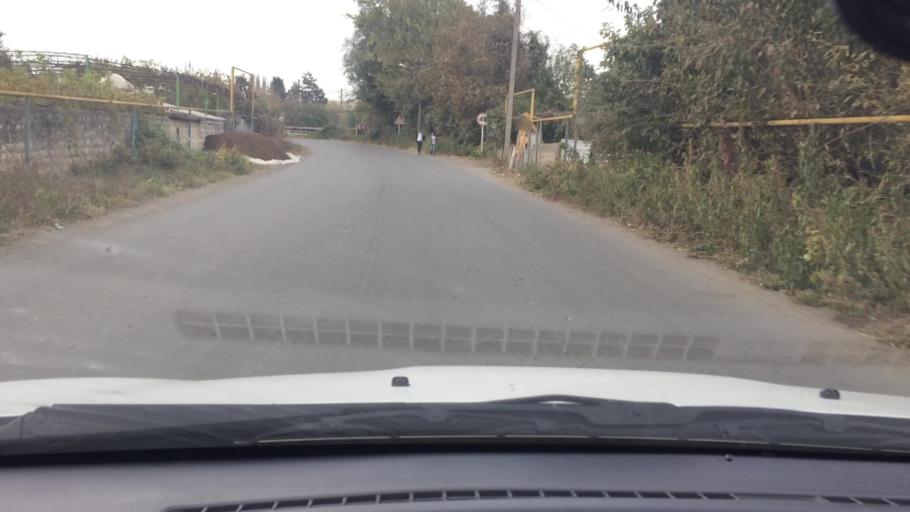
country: GE
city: Naghvarevi
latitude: 41.3530
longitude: 44.8627
